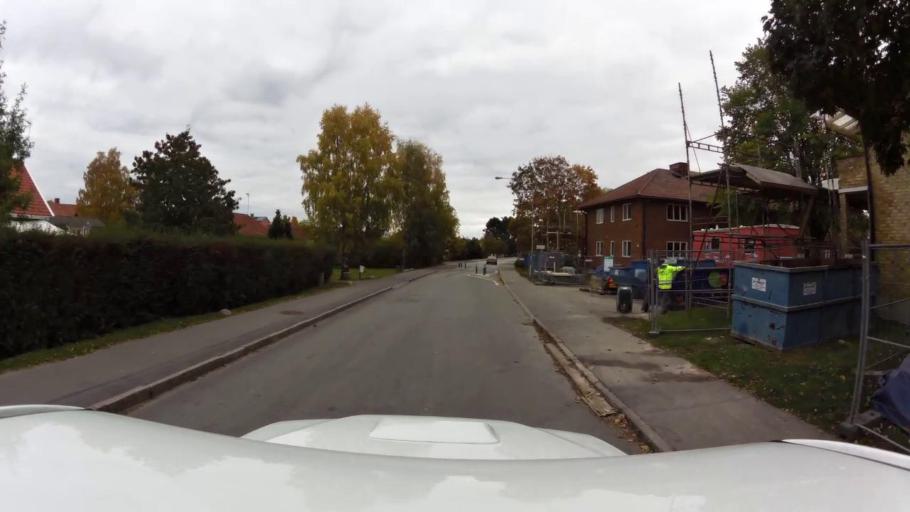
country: SE
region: OEstergoetland
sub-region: Linkopings Kommun
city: Ljungsbro
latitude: 58.5085
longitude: 15.5054
